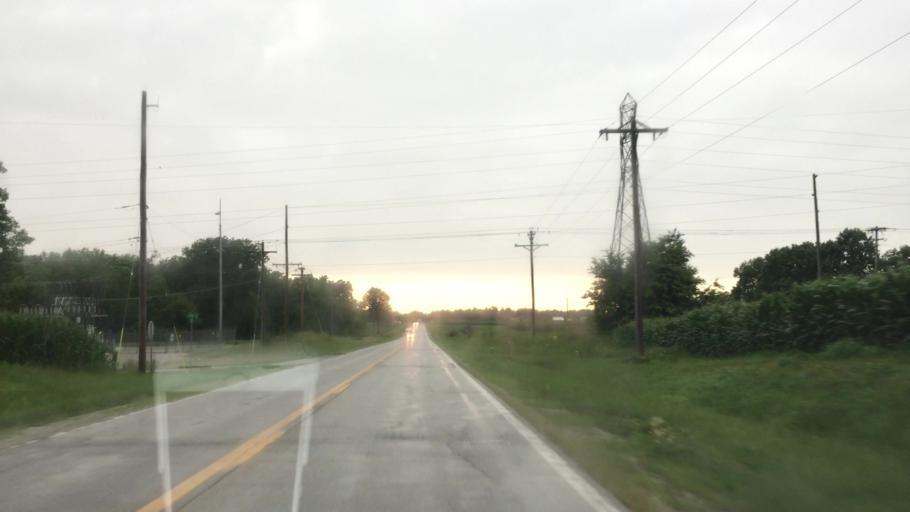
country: US
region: Illinois
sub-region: Hancock County
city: Nauvoo
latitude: 40.5522
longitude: -91.3506
